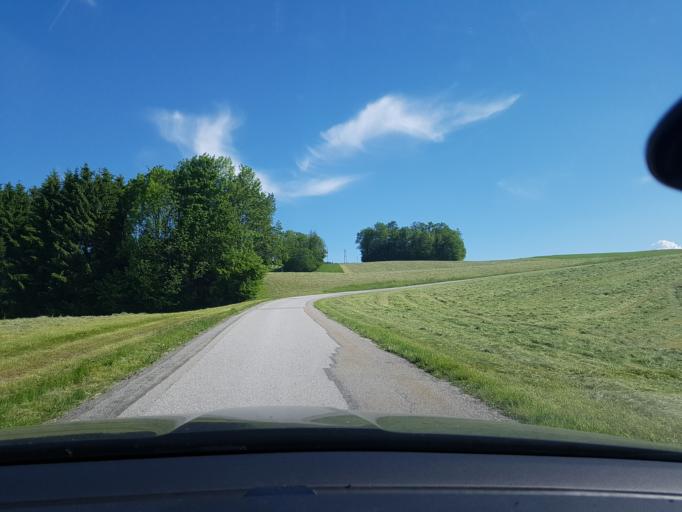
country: AT
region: Salzburg
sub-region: Politischer Bezirk Salzburg-Umgebung
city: Schleedorf
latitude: 47.9856
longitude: 13.1530
